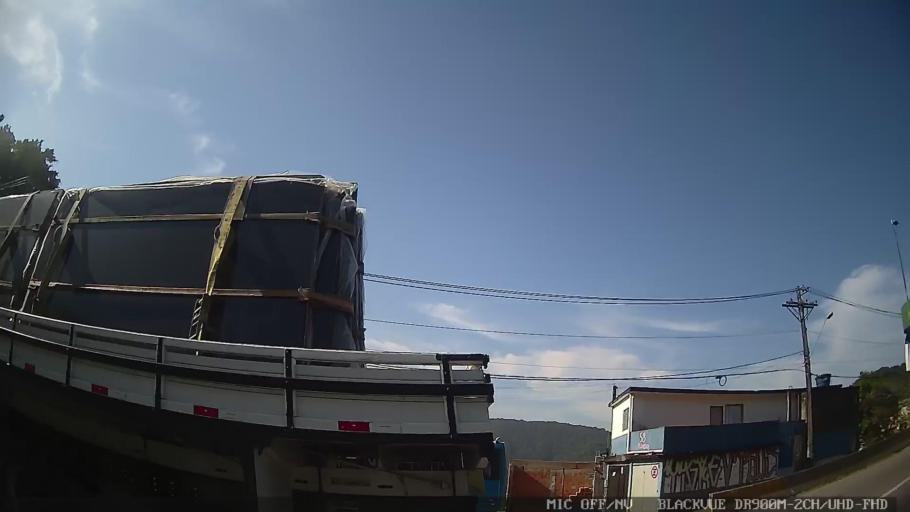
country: BR
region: Sao Paulo
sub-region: Cubatao
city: Cubatao
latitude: -23.8806
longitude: -46.4573
